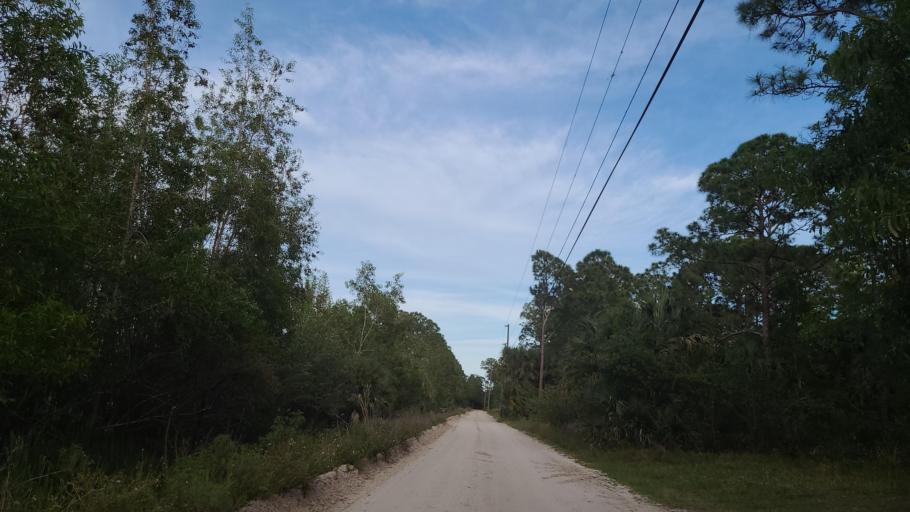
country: US
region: Florida
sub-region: Indian River County
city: Fellsmere
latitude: 27.7463
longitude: -80.5807
